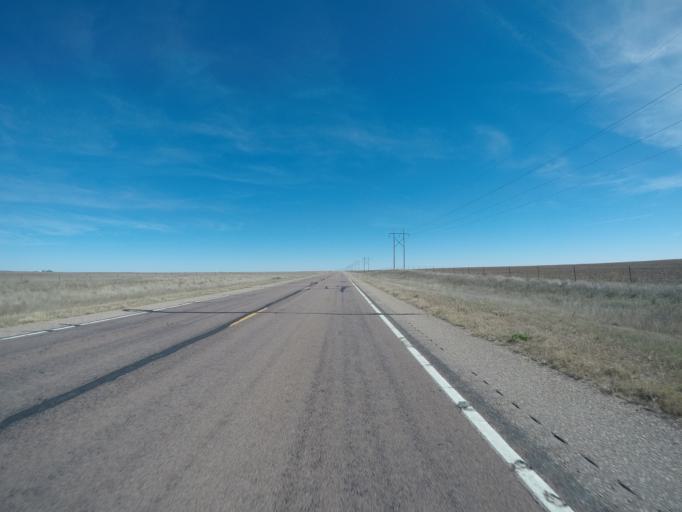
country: US
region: Colorado
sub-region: Yuma County
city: Yuma
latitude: 39.6549
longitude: -102.8154
